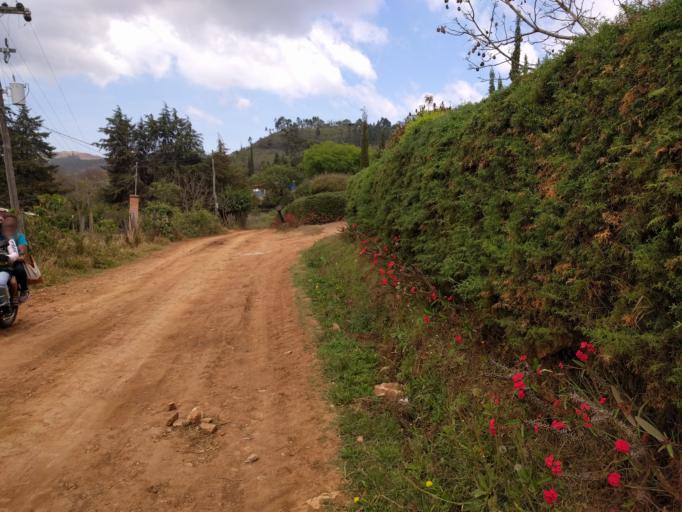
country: BO
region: Santa Cruz
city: Samaipata
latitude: -18.1860
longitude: -63.8777
